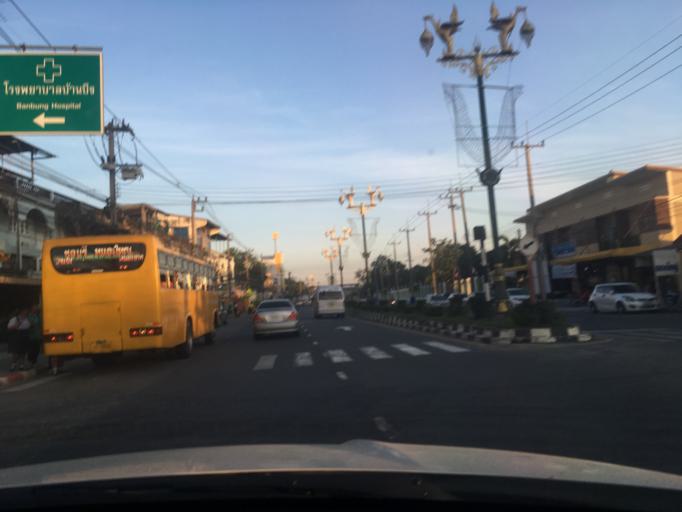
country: TH
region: Chon Buri
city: Ban Bueng
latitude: 13.3147
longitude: 101.1088
